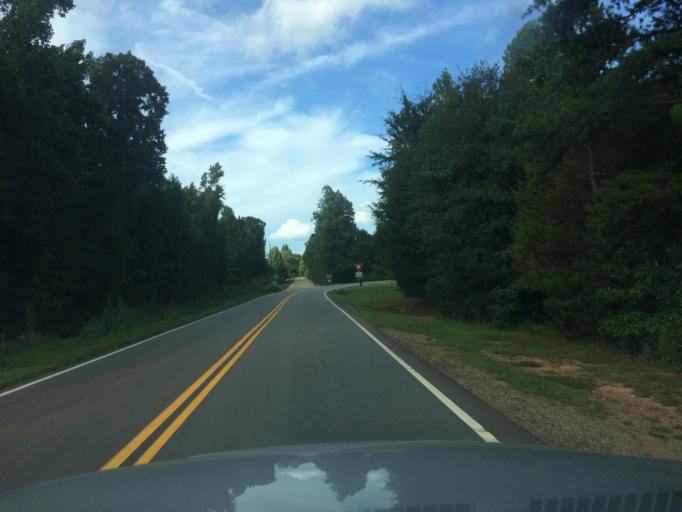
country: US
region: South Carolina
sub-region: Spartanburg County
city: Woodruff
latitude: 34.7559
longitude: -82.1054
